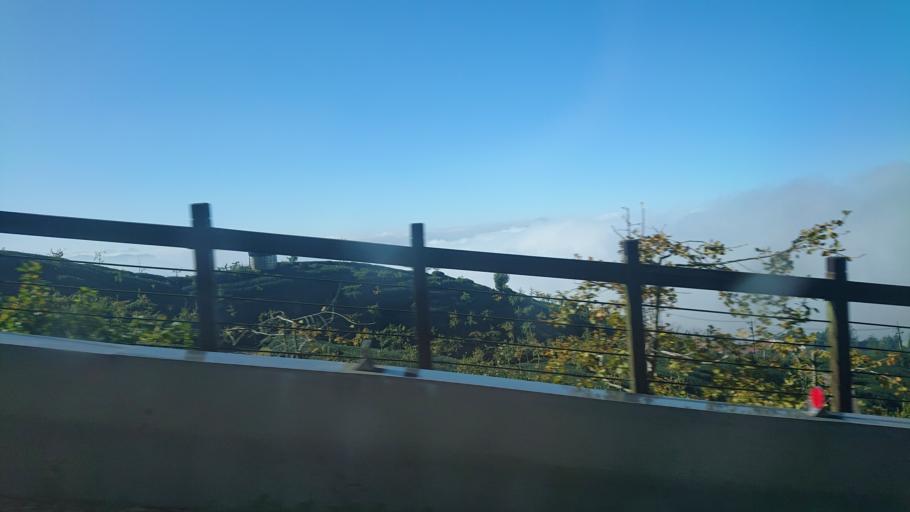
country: TW
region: Taiwan
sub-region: Chiayi
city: Jiayi Shi
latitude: 23.4793
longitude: 120.6999
